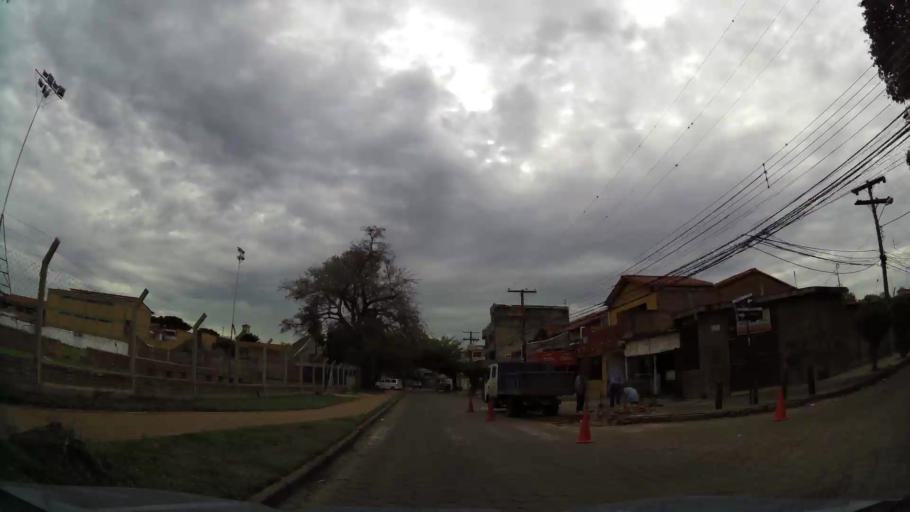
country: BO
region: Santa Cruz
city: Santa Cruz de la Sierra
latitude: -17.7747
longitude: -63.1713
